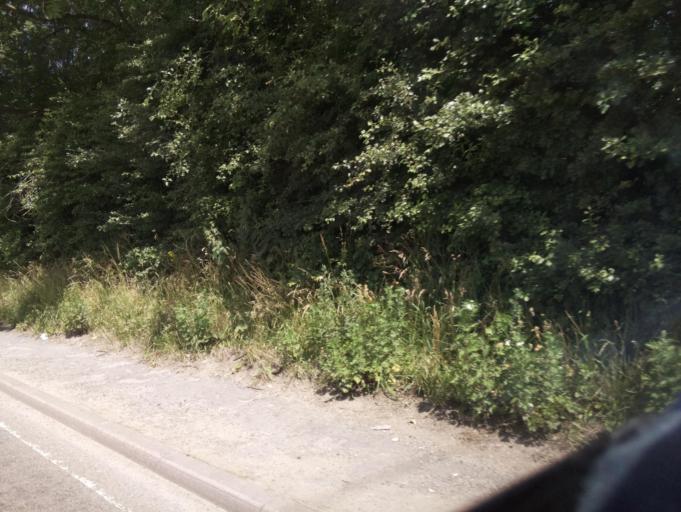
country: GB
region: England
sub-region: Derbyshire
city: Ashbourne
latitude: 53.0315
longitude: -1.7362
